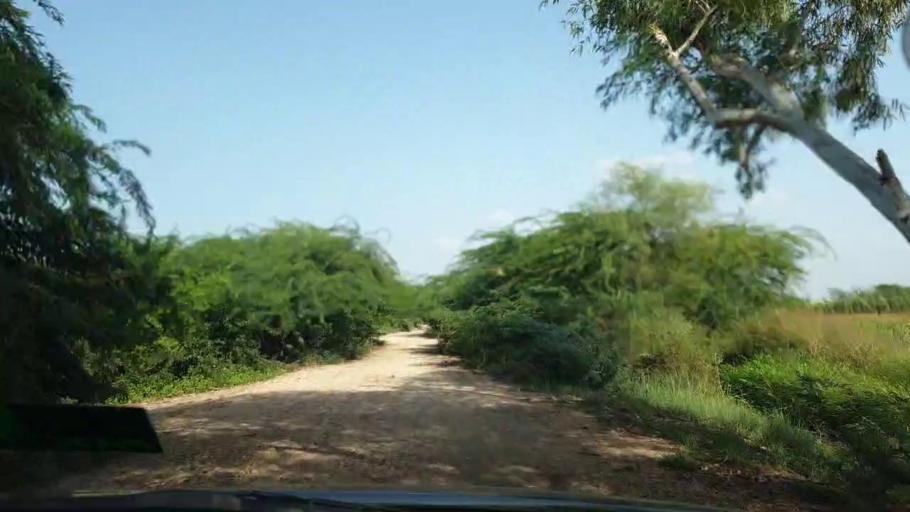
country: PK
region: Sindh
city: Tando Bago
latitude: 24.7000
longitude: 69.1957
